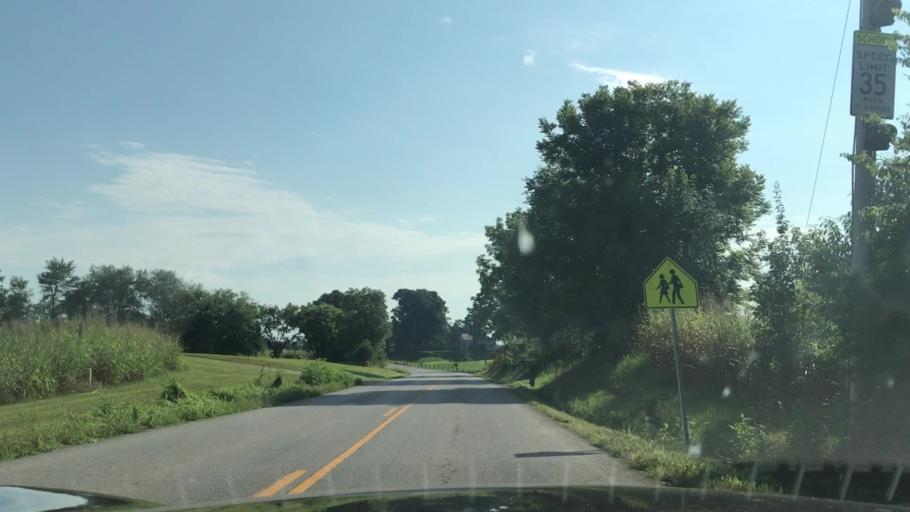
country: US
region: Kentucky
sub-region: Hart County
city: Horse Cave
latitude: 37.1682
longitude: -85.7969
